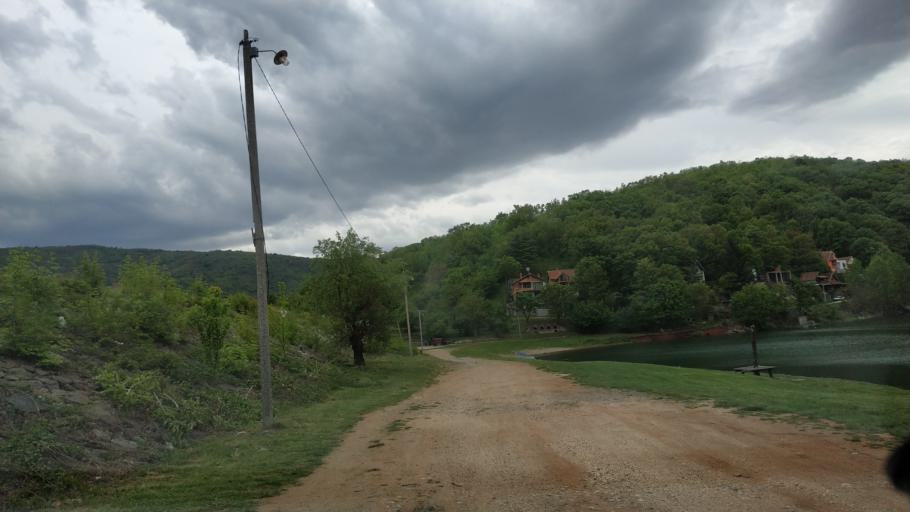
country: RS
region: Central Serbia
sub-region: Nisavski Okrug
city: Aleksinac
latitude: 43.6401
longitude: 21.7135
